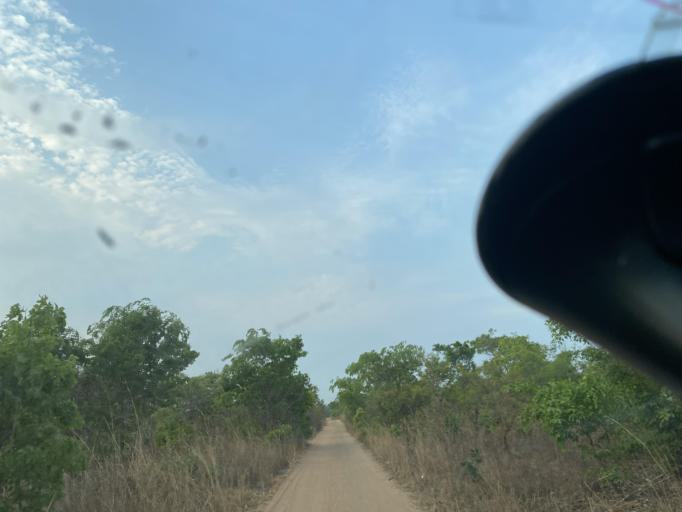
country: ZM
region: Lusaka
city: Chongwe
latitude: -15.2076
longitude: 28.5103
